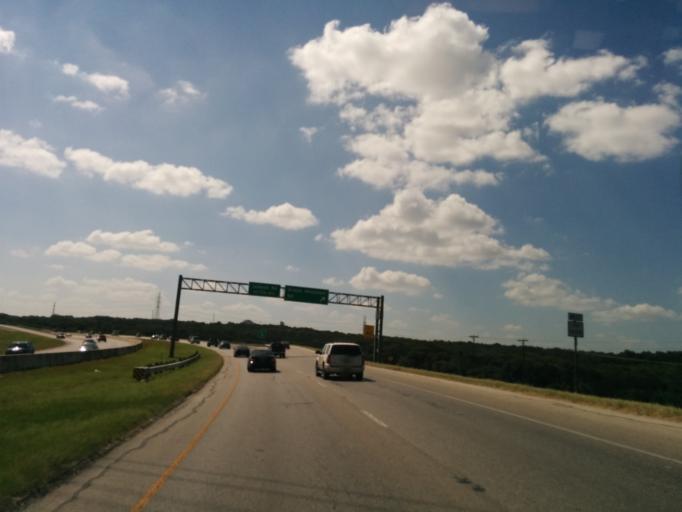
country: US
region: Texas
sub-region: Bexar County
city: Live Oak
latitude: 29.6019
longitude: -98.3594
